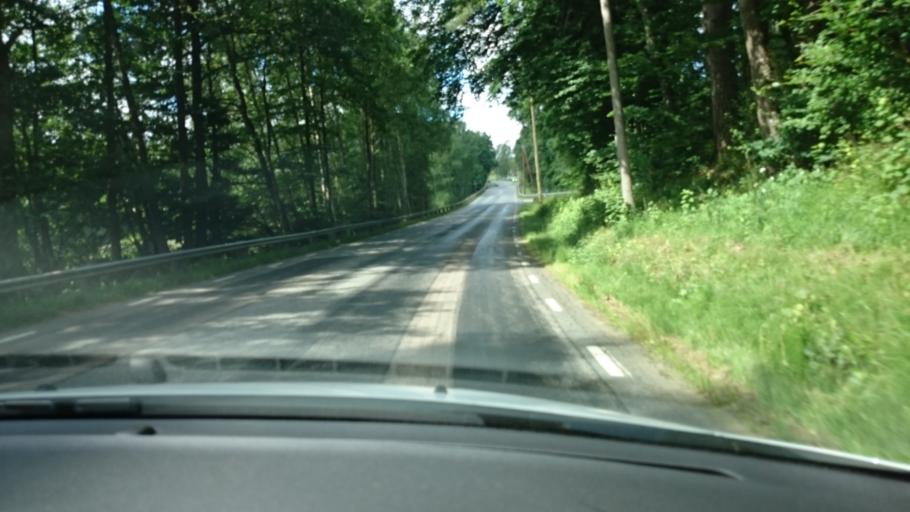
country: SE
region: Halland
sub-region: Hylte Kommun
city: Torup
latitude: 56.9571
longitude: 13.0959
